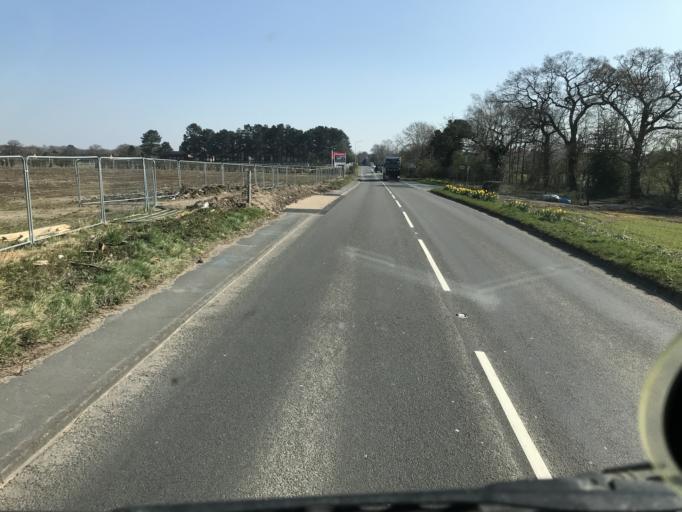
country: GB
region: England
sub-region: Cheshire East
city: Knutsford
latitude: 53.3028
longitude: -2.3916
